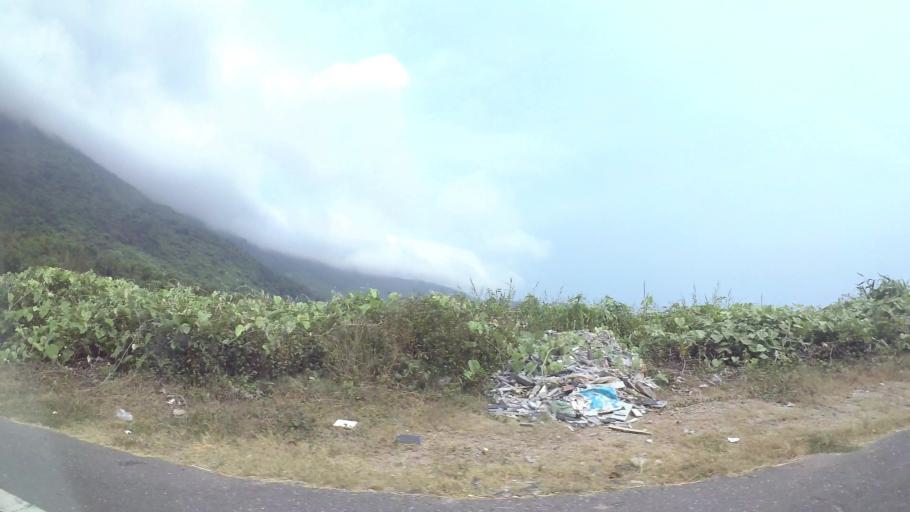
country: VN
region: Da Nang
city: Son Tra
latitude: 16.1010
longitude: 108.2811
